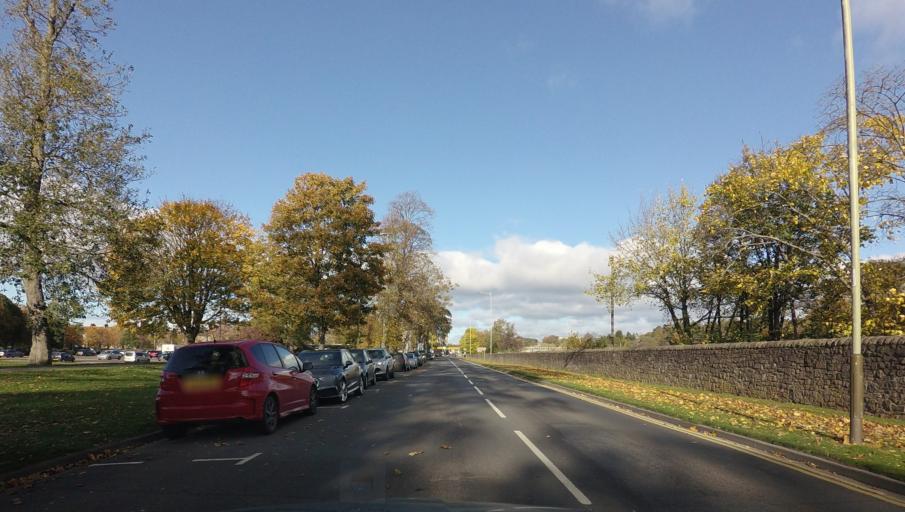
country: GB
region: Scotland
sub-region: Perth and Kinross
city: Perth
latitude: 56.3899
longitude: -3.4263
